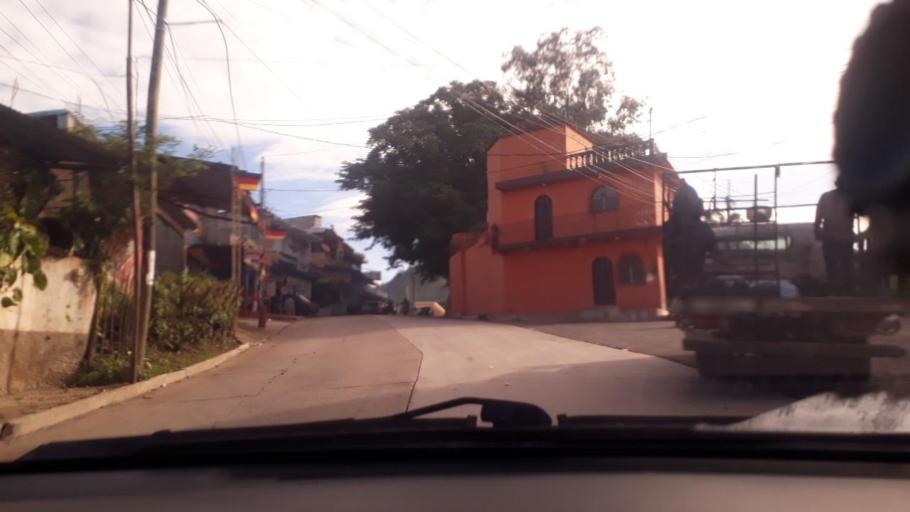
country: GT
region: Jutiapa
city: Jutiapa
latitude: 14.2984
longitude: -89.8942
